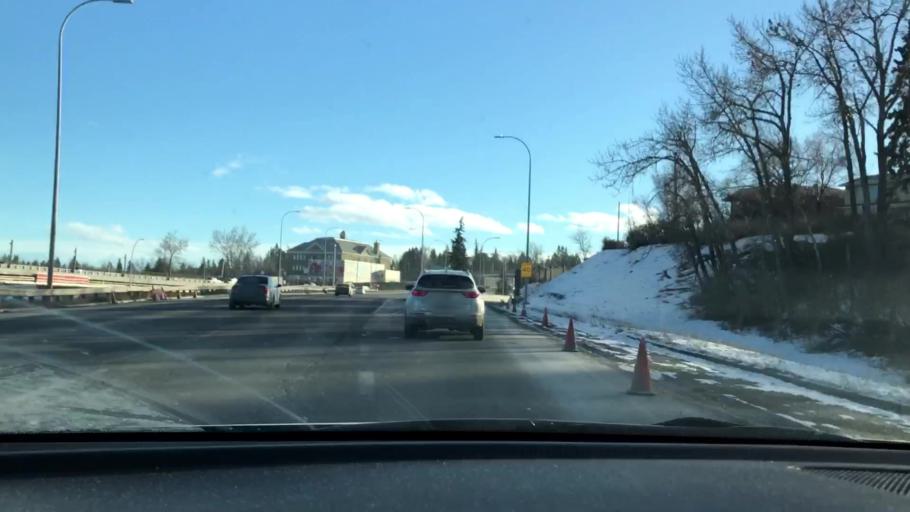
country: CA
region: Alberta
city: Calgary
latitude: 51.0444
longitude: -114.1136
